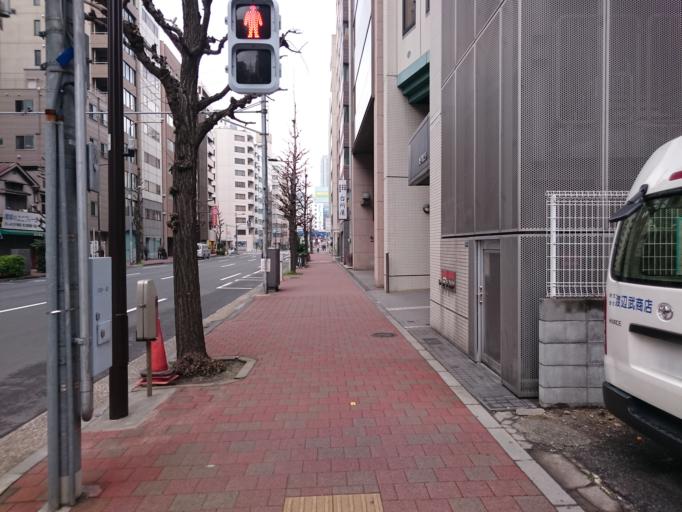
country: JP
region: Tokyo
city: Tokyo
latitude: 35.6935
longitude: 139.7769
